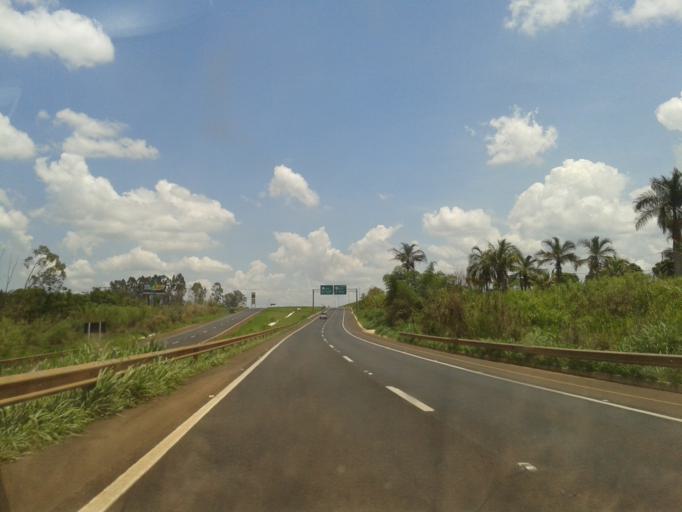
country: BR
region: Minas Gerais
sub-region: Uberlandia
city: Uberlandia
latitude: -18.8933
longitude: -48.4128
